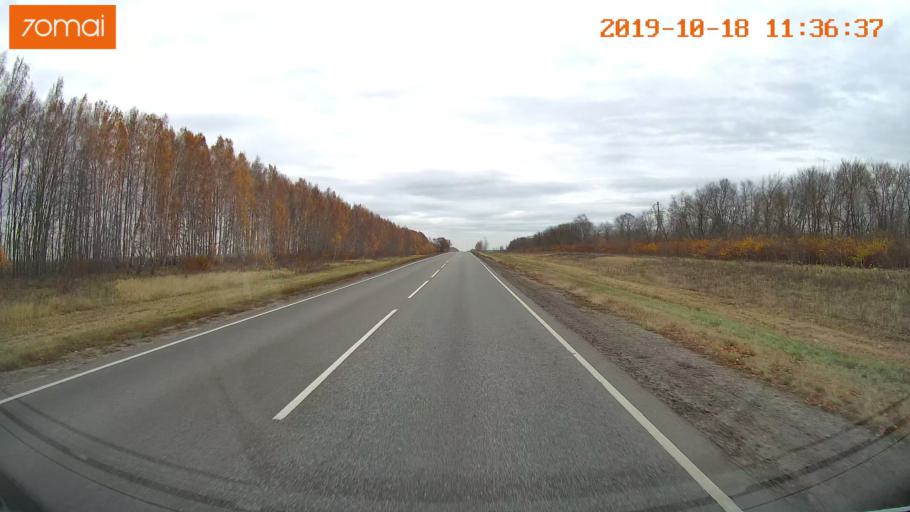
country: RU
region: Rjazan
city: Oktyabr'skiy
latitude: 54.1428
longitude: 38.8111
